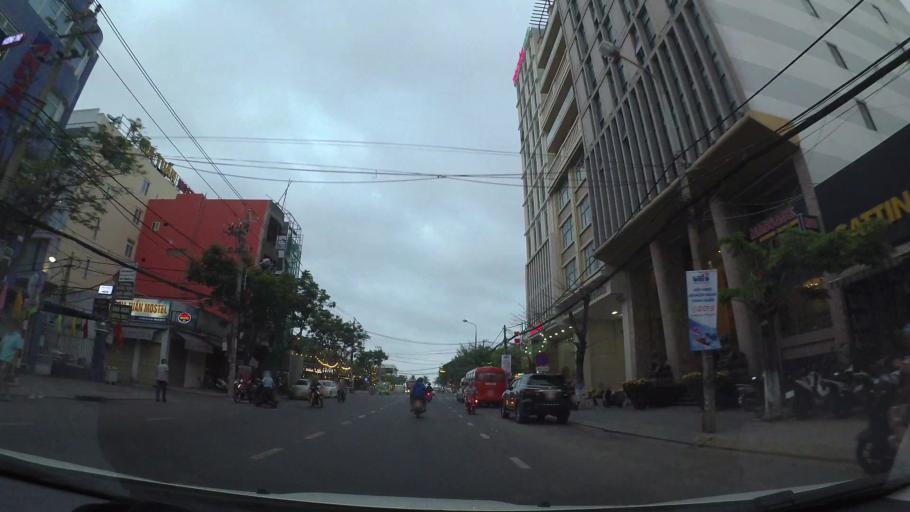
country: VN
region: Da Nang
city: Son Tra
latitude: 16.0559
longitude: 108.2450
